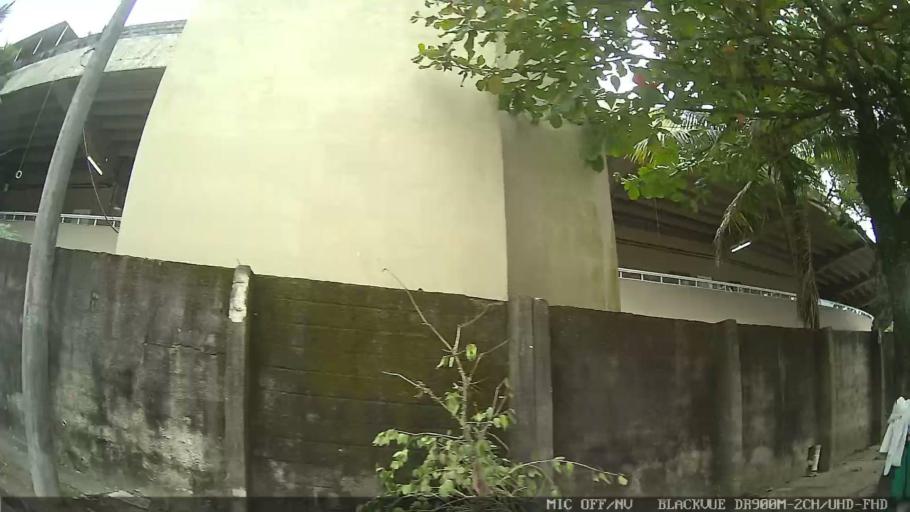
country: BR
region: Sao Paulo
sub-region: Guaruja
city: Guaruja
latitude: -23.9967
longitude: -46.2702
